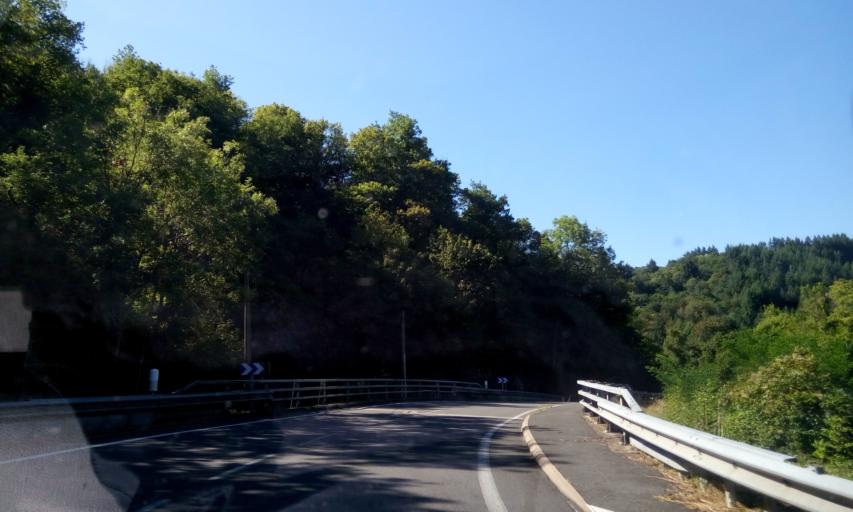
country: FR
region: Rhone-Alpes
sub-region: Departement du Rhone
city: Grandris
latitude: 45.9907
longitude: 4.5041
